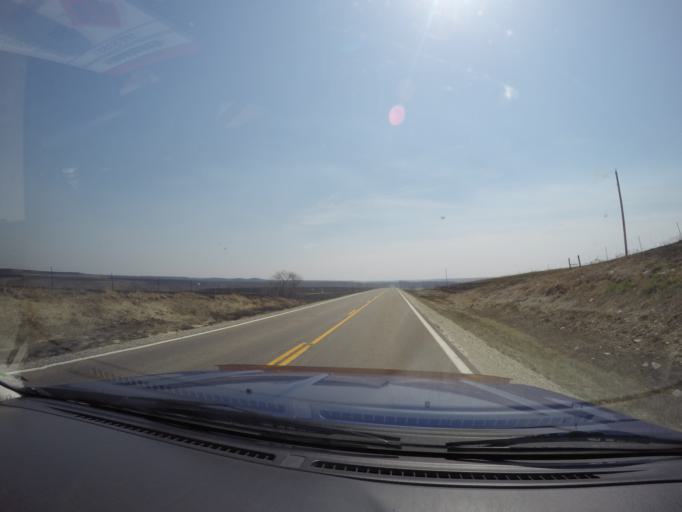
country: US
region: Kansas
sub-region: Chase County
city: Cottonwood Falls
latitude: 38.4910
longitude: -96.5573
